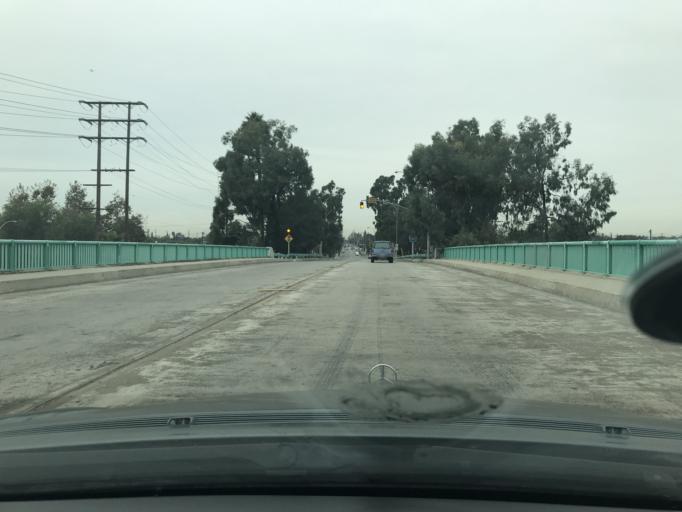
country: US
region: California
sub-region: Los Angeles County
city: Cudahy
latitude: 33.9639
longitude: -118.1711
